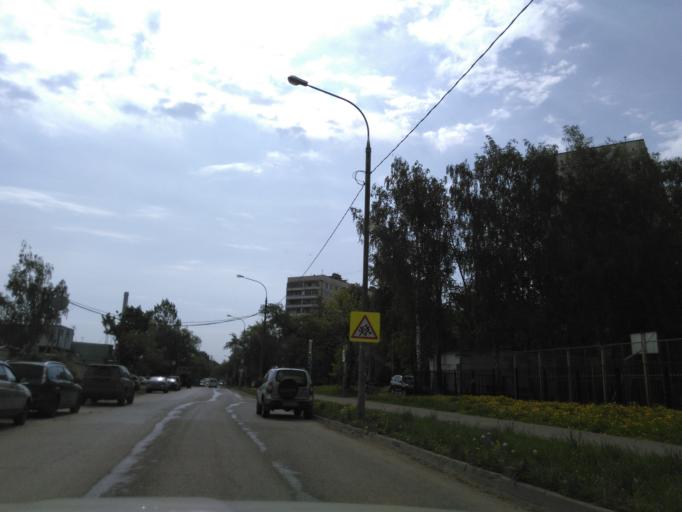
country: RU
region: Moscow
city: Novokhovrino
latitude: 55.8653
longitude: 37.5160
